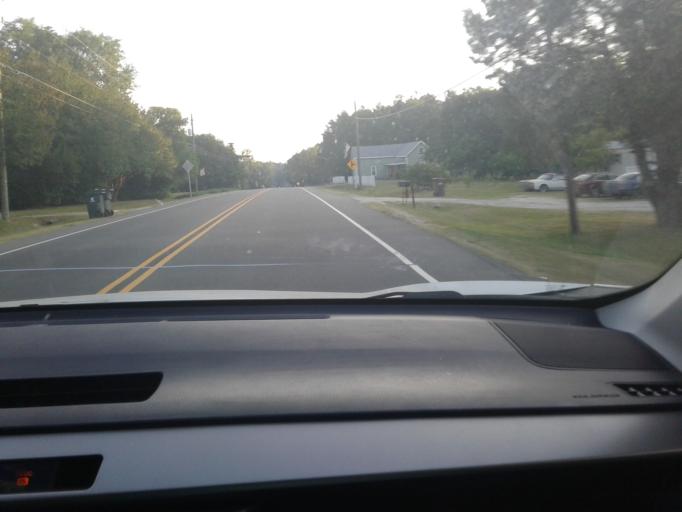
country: US
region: North Carolina
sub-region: Harnett County
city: Angier
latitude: 35.5096
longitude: -78.8136
